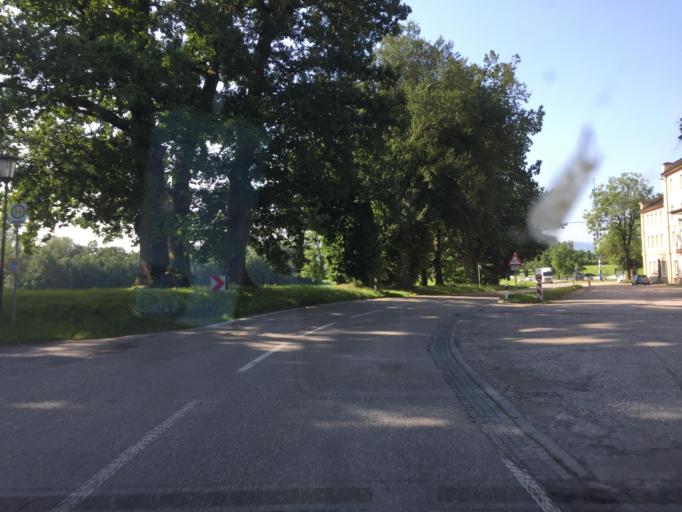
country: DE
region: Bavaria
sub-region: Upper Bavaria
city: Bad Aibling
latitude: 47.8993
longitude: 11.9891
